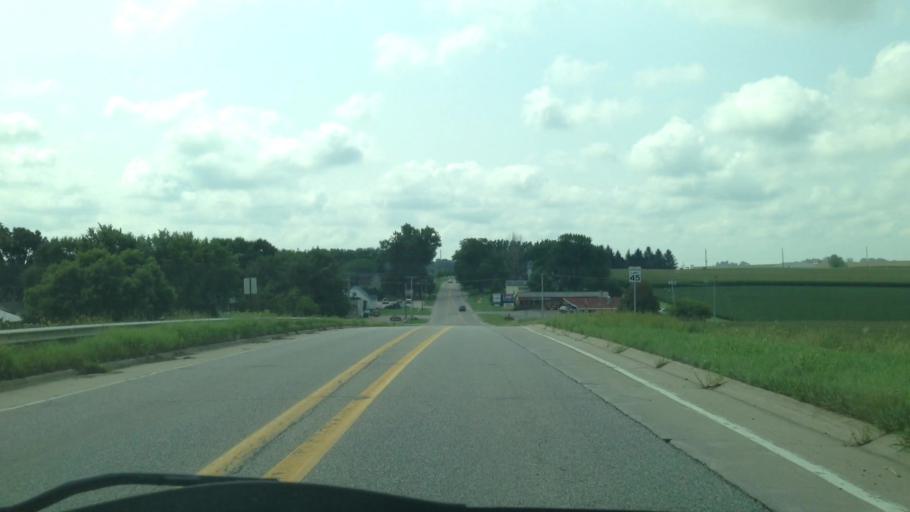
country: US
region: Iowa
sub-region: Linn County
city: Fairfax
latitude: 41.9199
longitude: -91.7838
